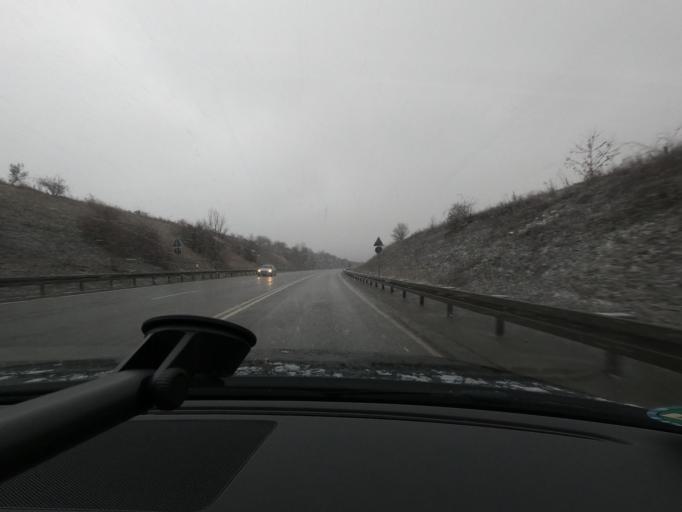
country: DE
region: Thuringia
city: Dingelstadt
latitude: 51.3270
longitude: 10.3278
